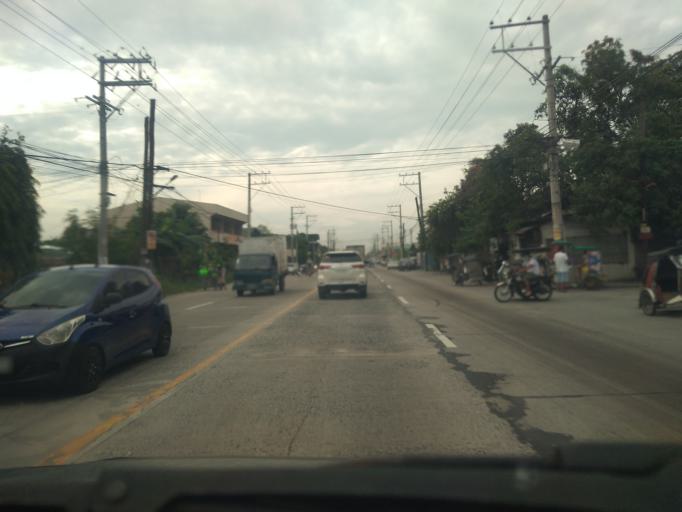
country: PH
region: Central Luzon
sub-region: Province of Pampanga
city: Del Pilar
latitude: 15.0303
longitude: 120.6967
